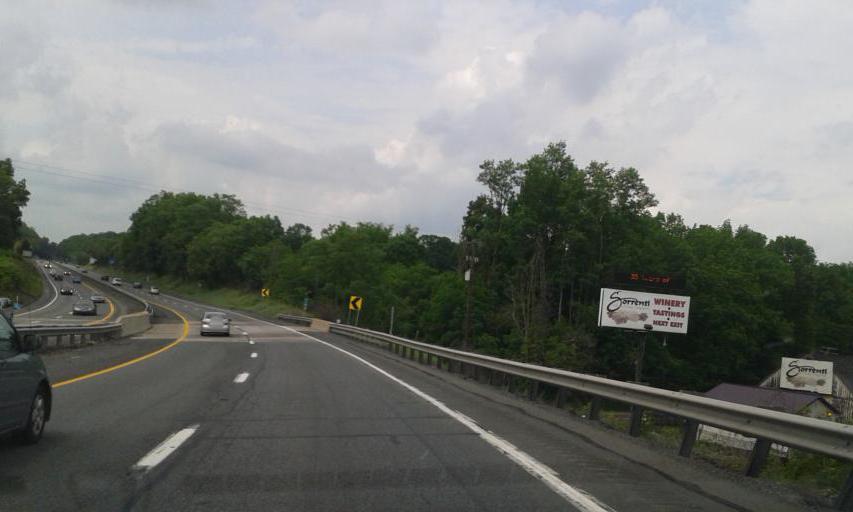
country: US
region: Pennsylvania
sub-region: Monroe County
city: Saylorsburg
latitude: 40.8844
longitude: -75.3086
